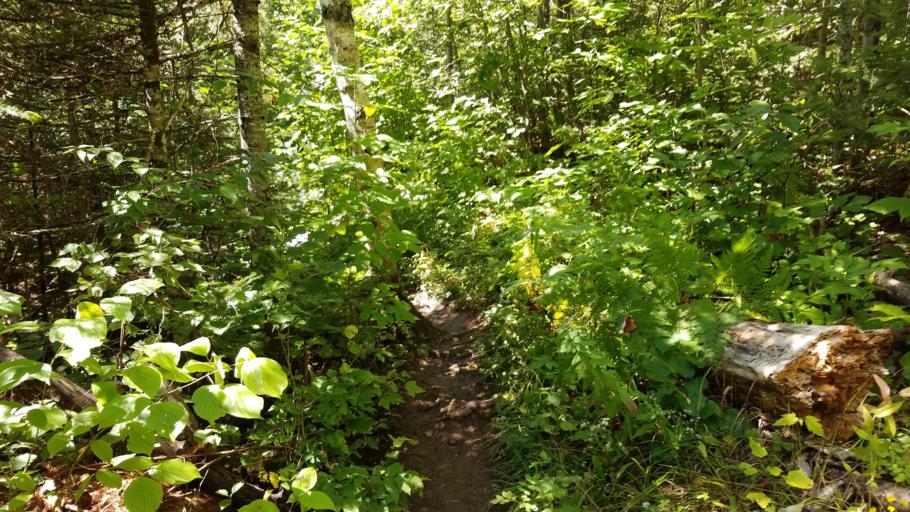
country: US
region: Michigan
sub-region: Ontonagon County
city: Ontonagon
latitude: 46.6515
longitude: -89.1590
